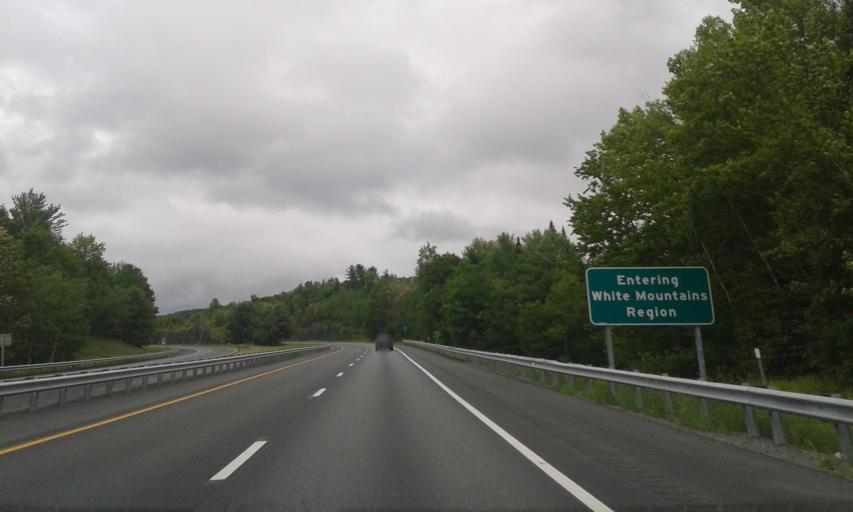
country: US
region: New Hampshire
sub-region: Grafton County
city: Littleton
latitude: 44.3143
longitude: -71.8563
